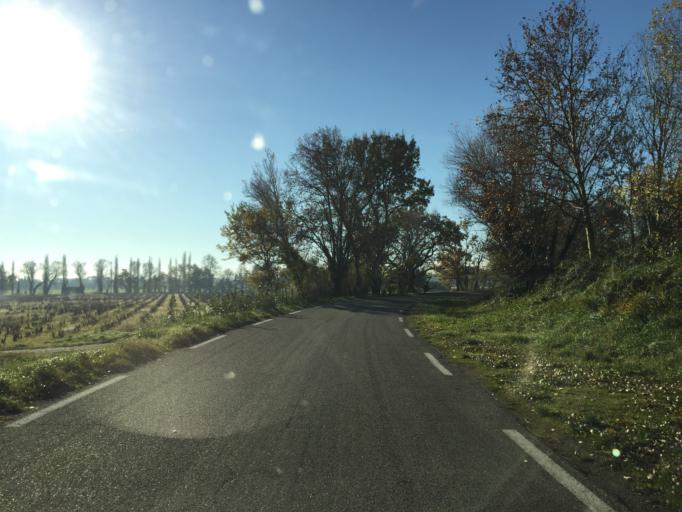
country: FR
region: Provence-Alpes-Cote d'Azur
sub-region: Departement du Vaucluse
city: Bedarrides
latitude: 44.0415
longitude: 4.9308
